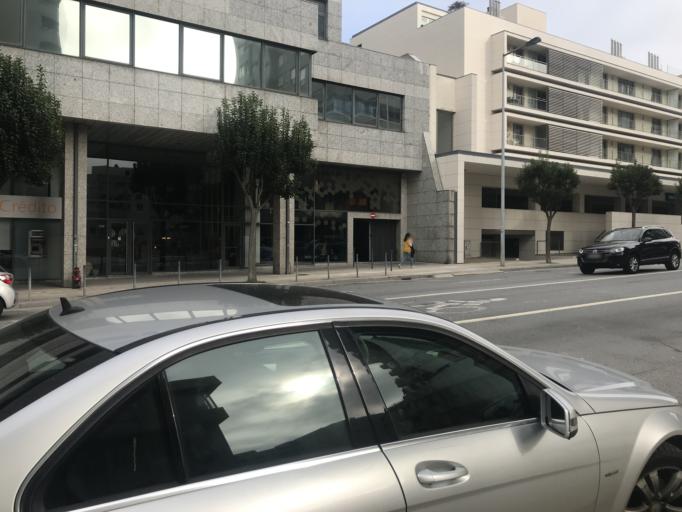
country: PT
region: Porto
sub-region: Porto
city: Porto
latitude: 41.1502
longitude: -8.6258
